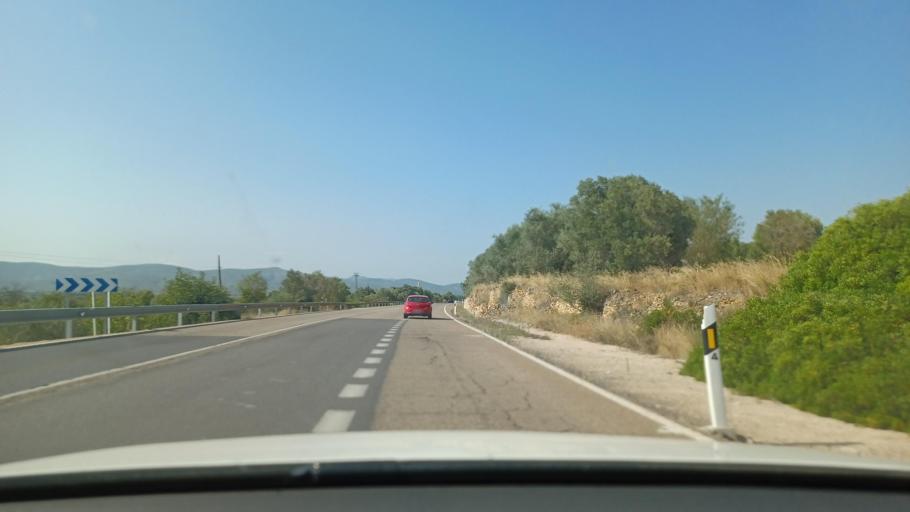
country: ES
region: Valencia
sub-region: Provincia de Castello
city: Alcala de Xivert
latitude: 40.2841
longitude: 0.2246
